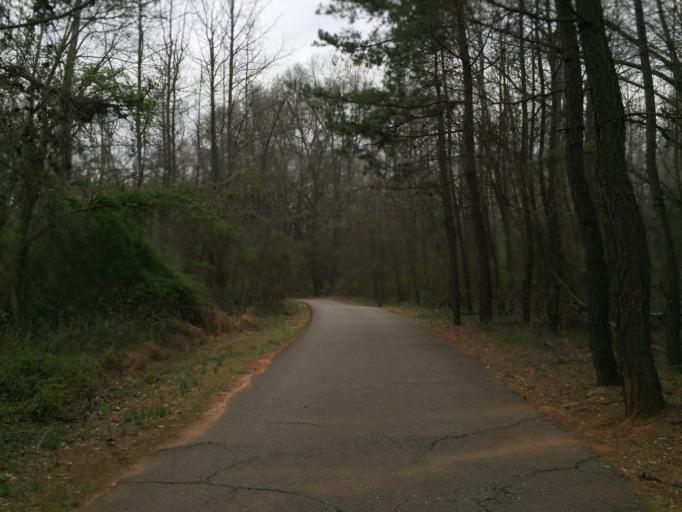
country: US
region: South Carolina
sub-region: Greenville County
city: Mauldin
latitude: 34.7771
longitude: -82.3595
